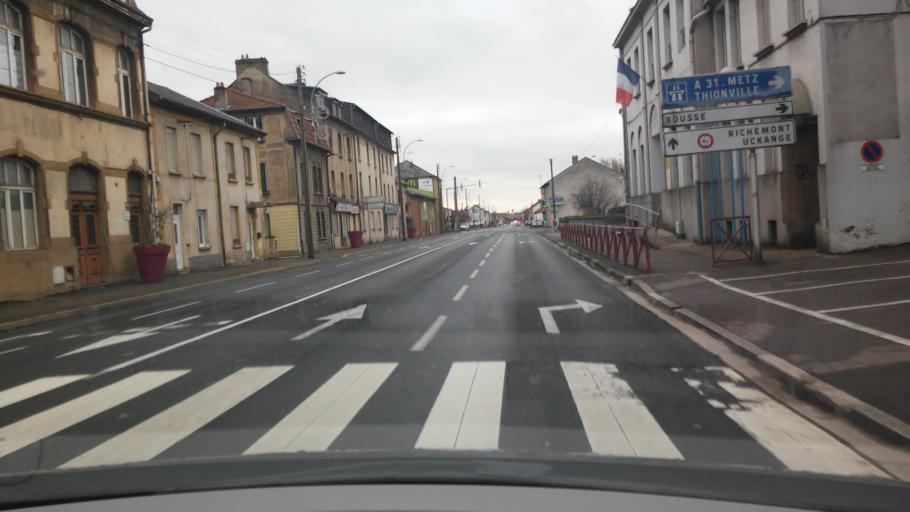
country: FR
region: Lorraine
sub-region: Departement de la Moselle
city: Mondelange
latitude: 49.2621
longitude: 6.1700
